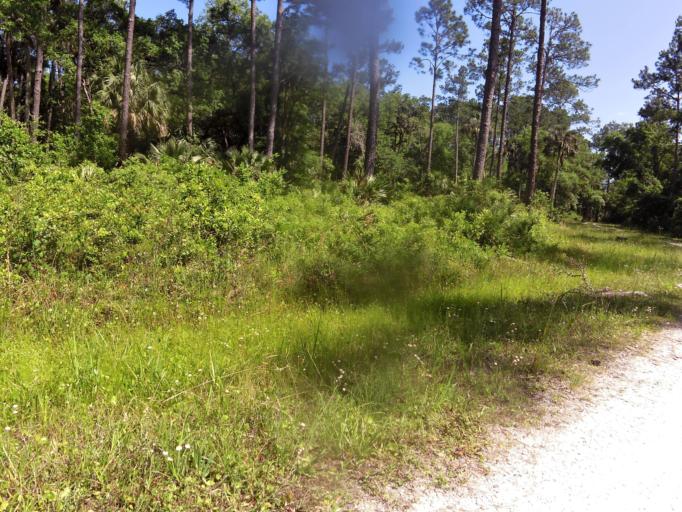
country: US
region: Florida
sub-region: Saint Johns County
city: Palm Valley
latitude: 30.1384
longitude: -81.3777
